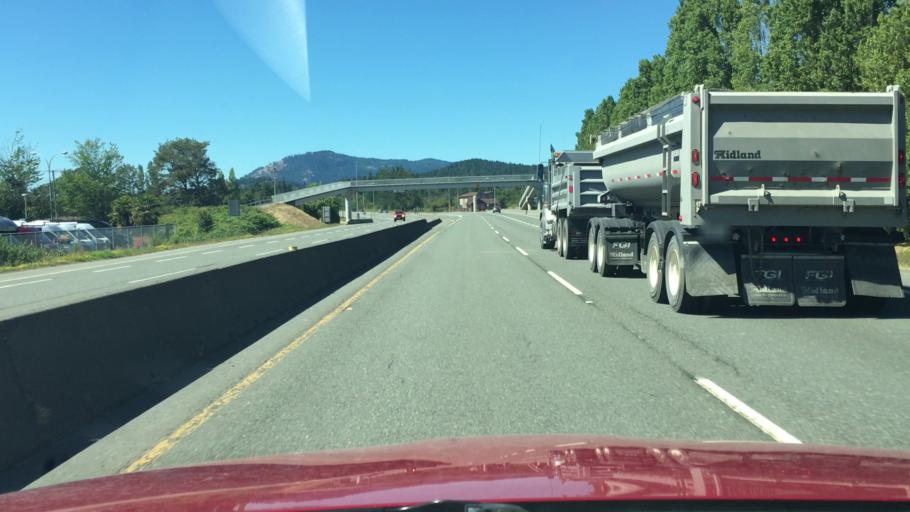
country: CA
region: British Columbia
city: North Saanich
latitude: 48.6606
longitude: -123.4155
